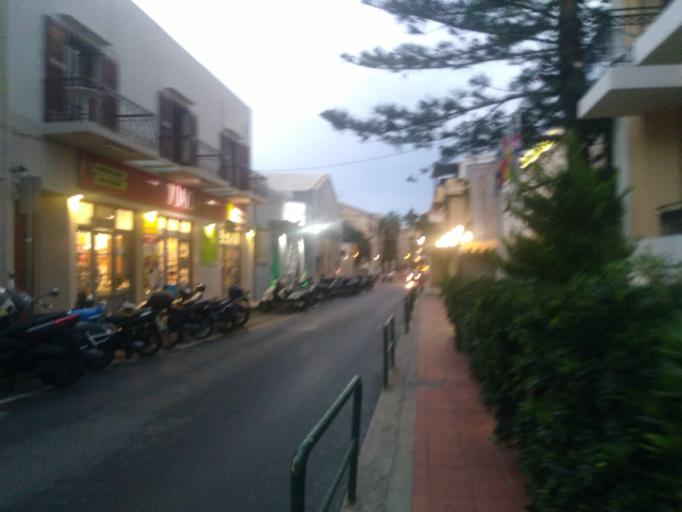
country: GR
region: Crete
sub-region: Nomos Rethymnis
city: Rethymno
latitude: 35.3707
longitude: 24.4735
